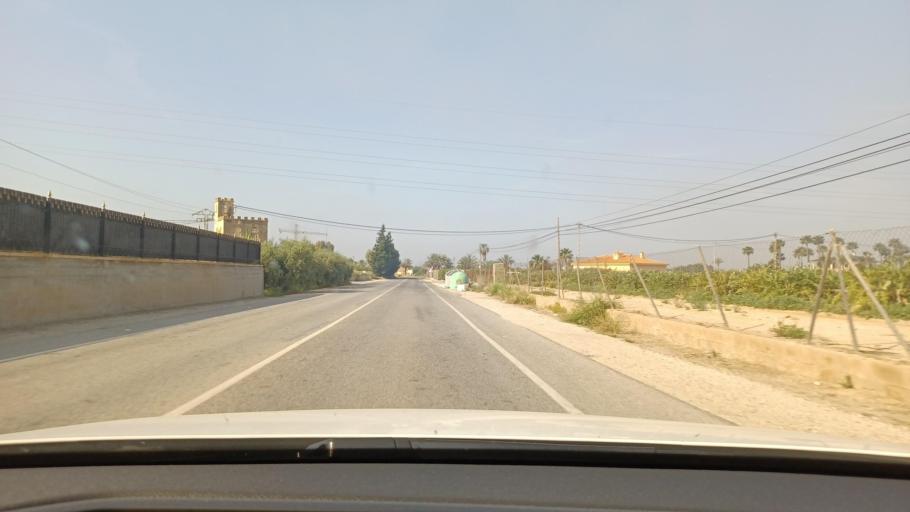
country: ES
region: Valencia
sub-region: Provincia de Alicante
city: Elche
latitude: 38.2352
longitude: -0.7154
